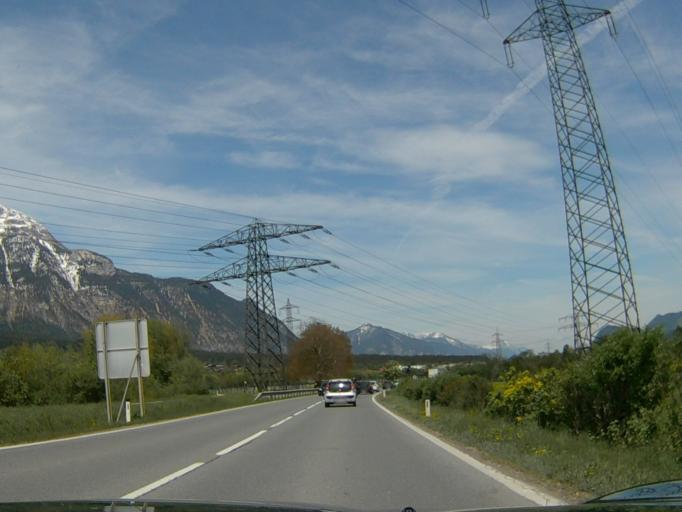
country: AT
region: Tyrol
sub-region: Politischer Bezirk Schwaz
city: Wiesing
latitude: 47.3941
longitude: 11.7991
